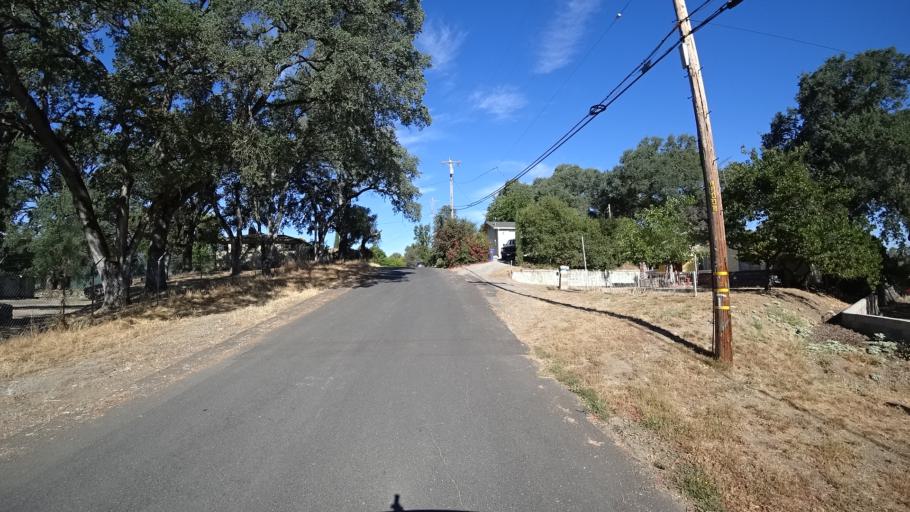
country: US
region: California
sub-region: Calaveras County
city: San Andreas
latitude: 38.1924
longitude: -120.6712
